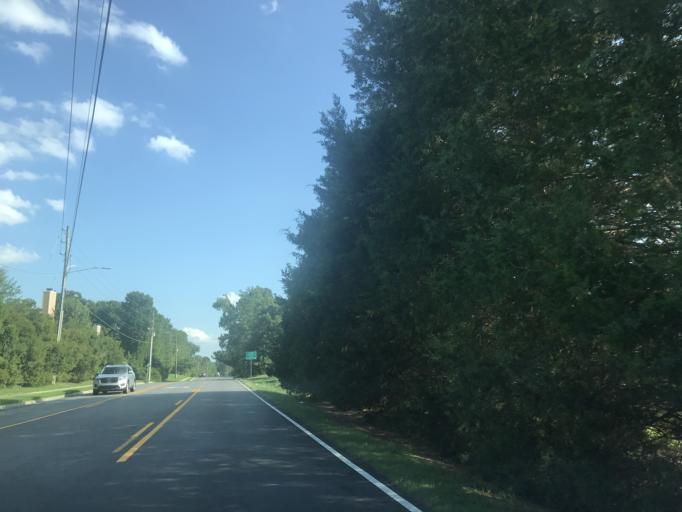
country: US
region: North Carolina
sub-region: Wake County
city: Knightdale
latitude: 35.7875
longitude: -78.5468
